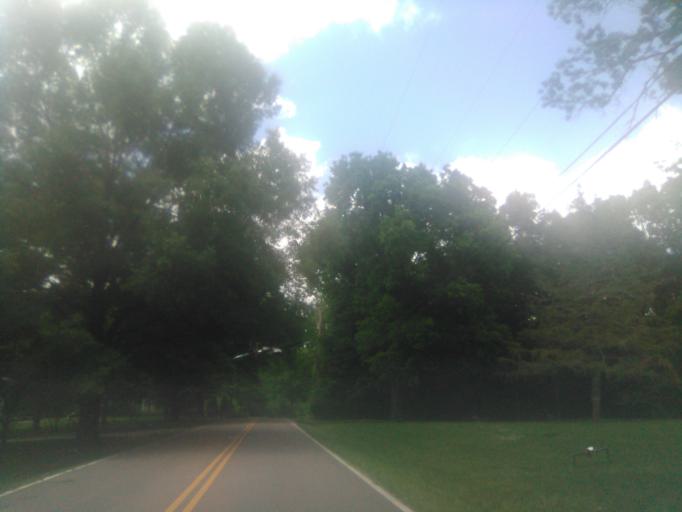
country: US
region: Tennessee
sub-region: Davidson County
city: Belle Meade
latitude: 36.1078
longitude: -86.8465
